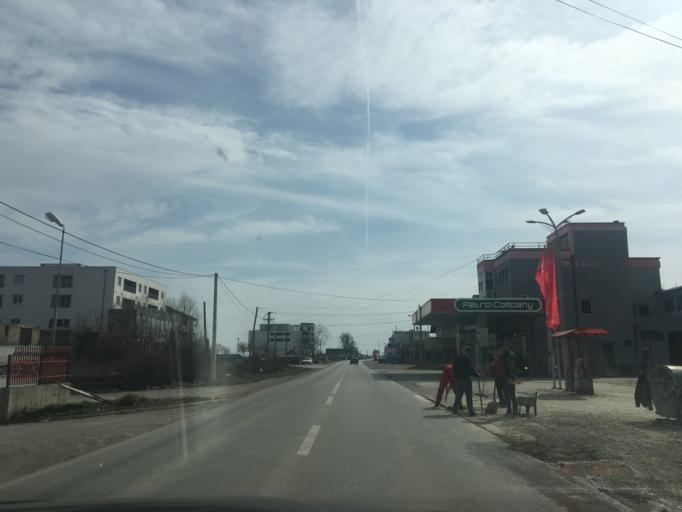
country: XK
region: Pec
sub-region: Komuna e Pejes
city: Peje
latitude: 42.6374
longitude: 20.2984
